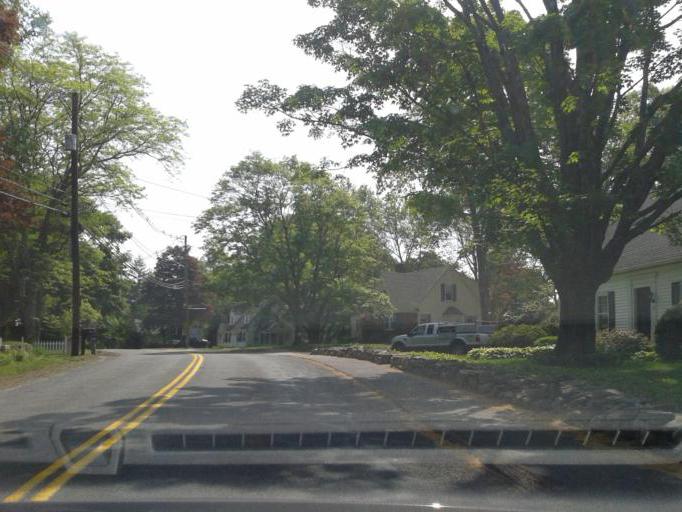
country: US
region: Massachusetts
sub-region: Worcester County
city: Westborough
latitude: 42.2707
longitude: -71.6251
